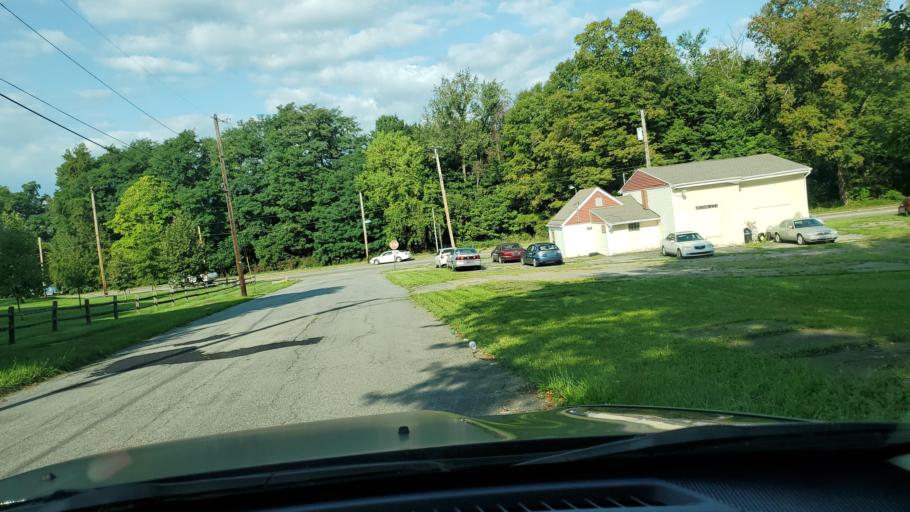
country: US
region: Ohio
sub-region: Mahoning County
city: Youngstown
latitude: 41.0870
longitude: -80.6716
